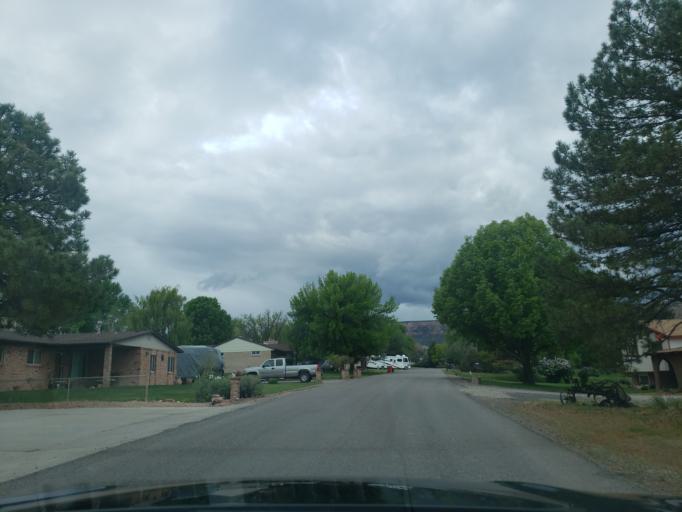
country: US
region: Colorado
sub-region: Mesa County
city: Redlands
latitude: 39.0995
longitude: -108.6616
